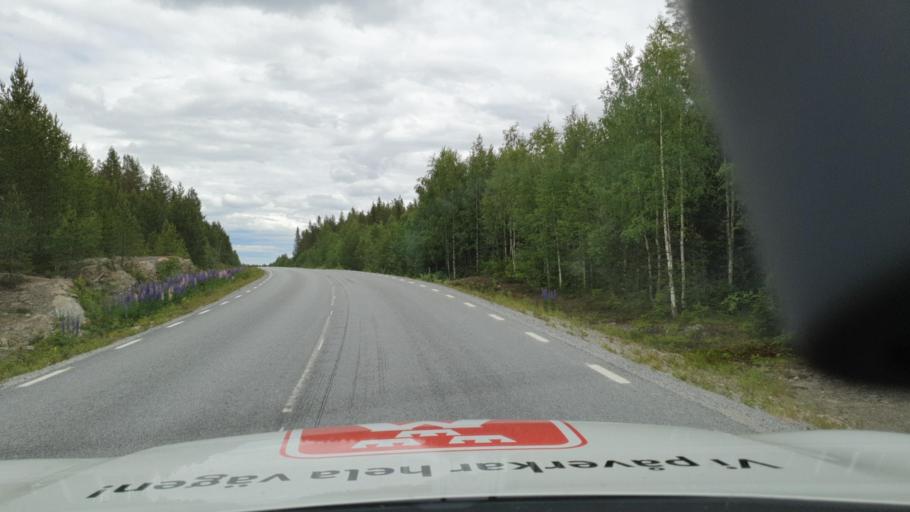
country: SE
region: Vaesterbotten
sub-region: Bjurholms Kommun
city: Bjurholm
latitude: 63.8823
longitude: 19.0338
